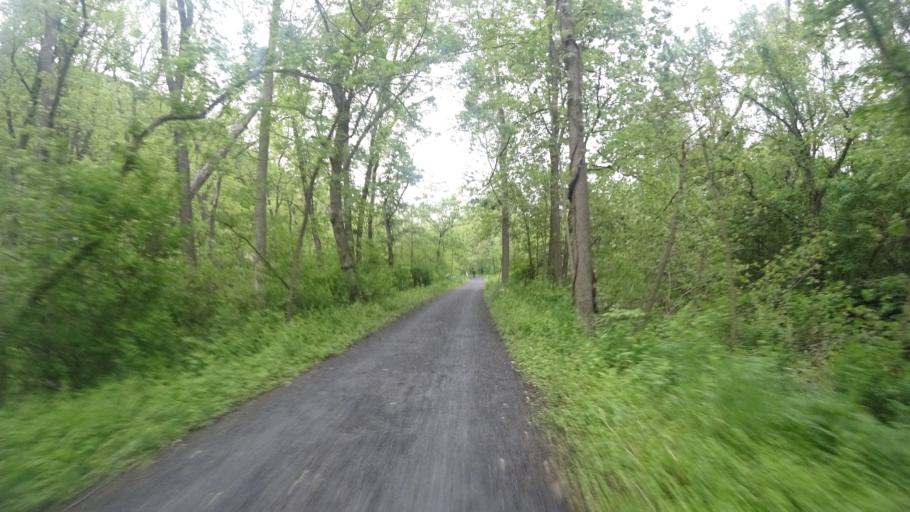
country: US
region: Maryland
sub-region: Frederick County
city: Brunswick
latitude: 39.3294
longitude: -77.6789
